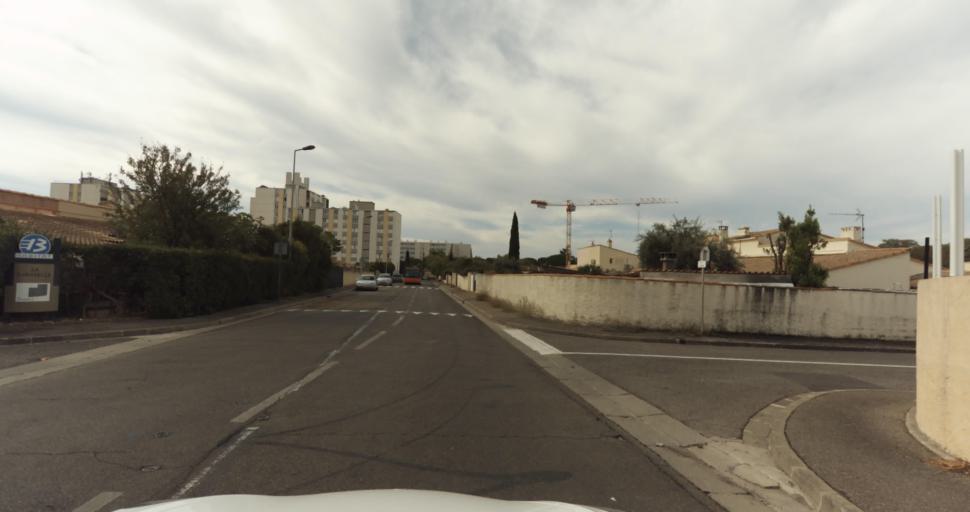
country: FR
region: Provence-Alpes-Cote d'Azur
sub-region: Departement des Bouches-du-Rhone
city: Miramas
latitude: 43.5937
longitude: 5.0058
